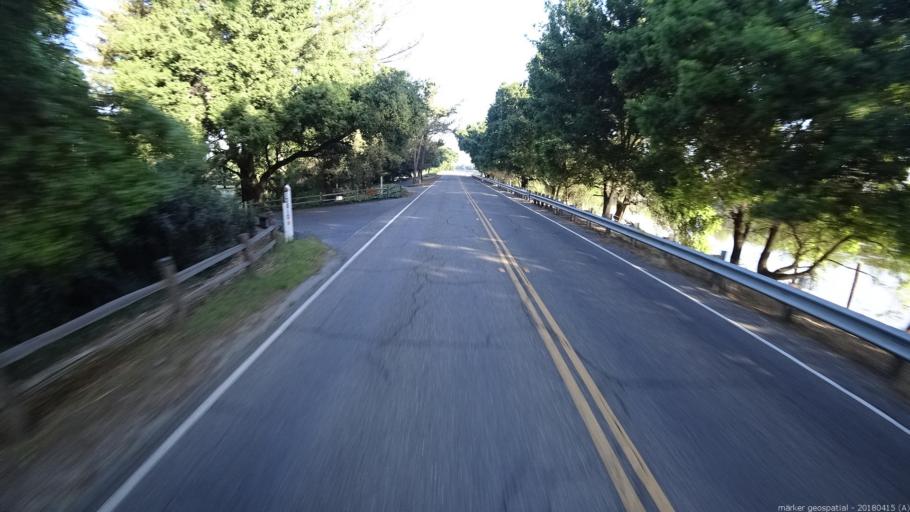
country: US
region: California
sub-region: Sacramento County
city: Walnut Grove
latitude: 38.2544
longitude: -121.5146
